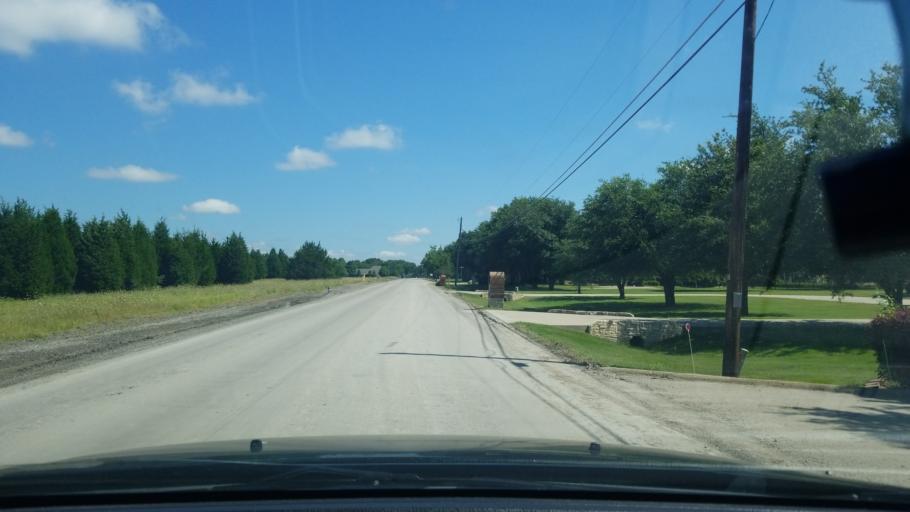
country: US
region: Texas
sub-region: Dallas County
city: Sunnyvale
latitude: 32.7919
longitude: -96.5796
